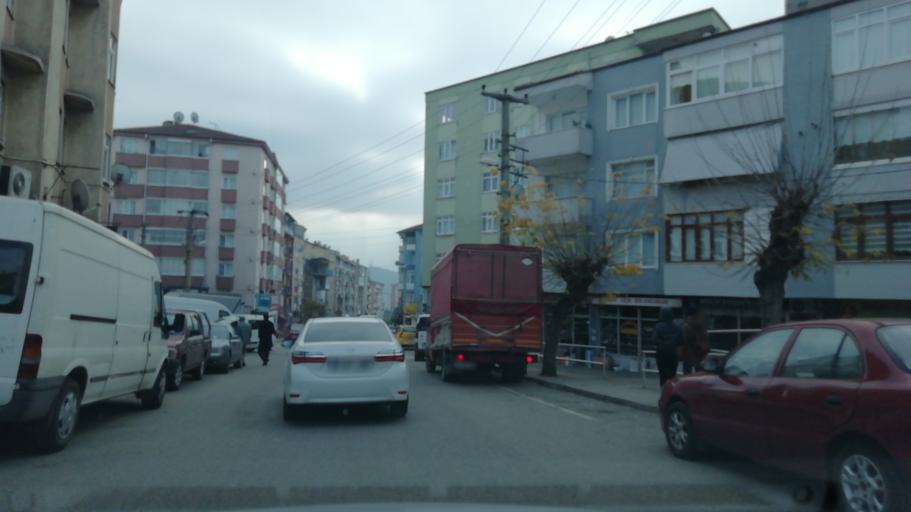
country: TR
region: Karabuk
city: Karabuk
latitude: 41.2072
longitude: 32.6265
